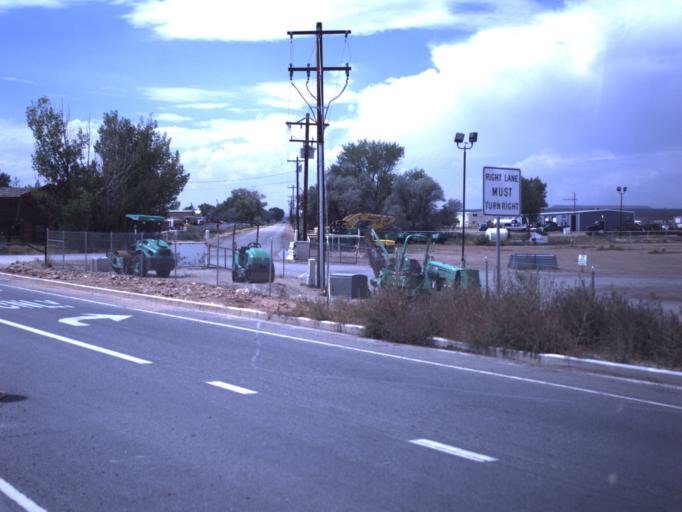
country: US
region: Utah
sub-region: Duchesne County
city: Roosevelt
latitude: 40.2732
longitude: -110.0307
